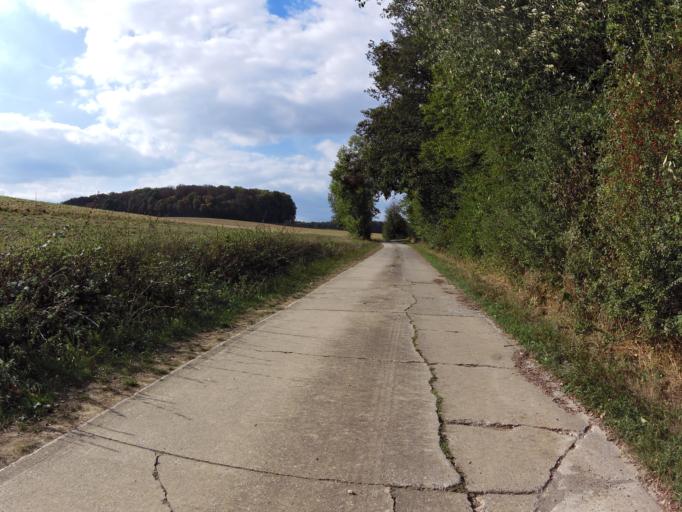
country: DE
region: Bavaria
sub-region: Regierungsbezirk Unterfranken
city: Hettstadt
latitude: 49.7832
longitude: 9.7989
